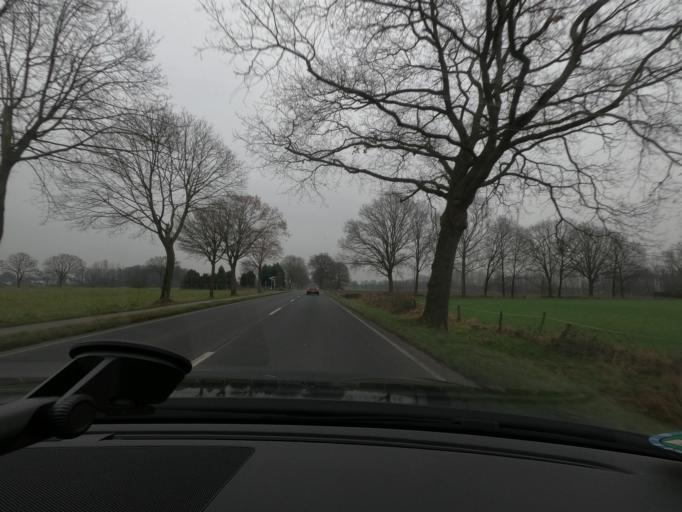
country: DE
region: North Rhine-Westphalia
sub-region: Regierungsbezirk Dusseldorf
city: Wachtendonk
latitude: 51.3965
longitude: 6.2898
